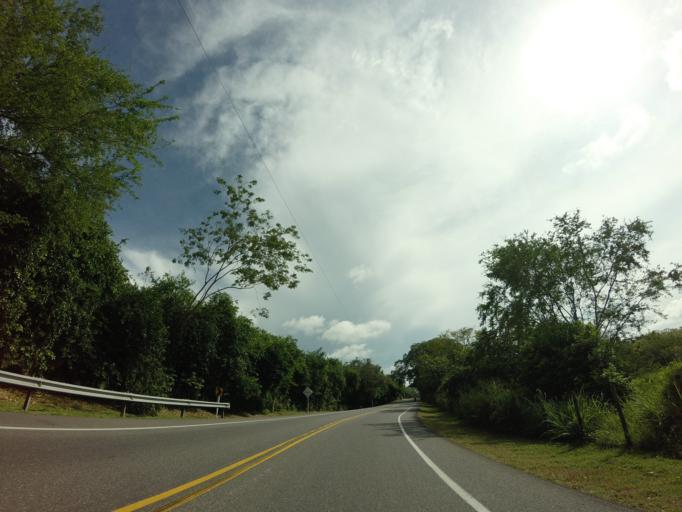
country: CO
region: Tolima
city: Honda
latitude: 5.2902
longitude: -74.7466
